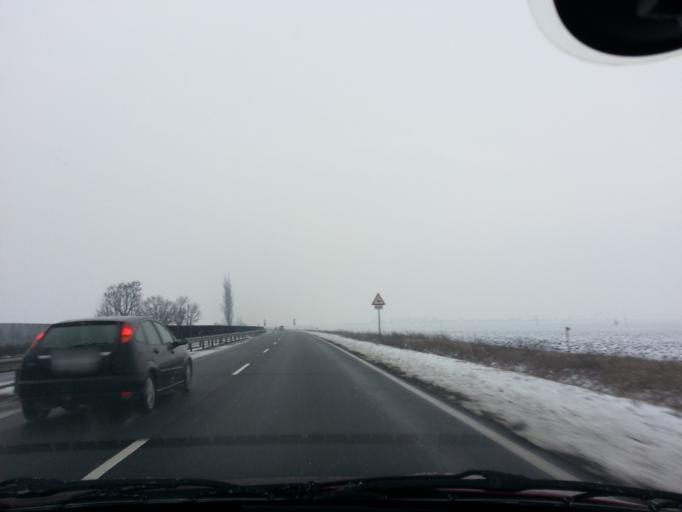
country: HU
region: Heves
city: Lorinci
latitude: 47.7411
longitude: 19.6628
